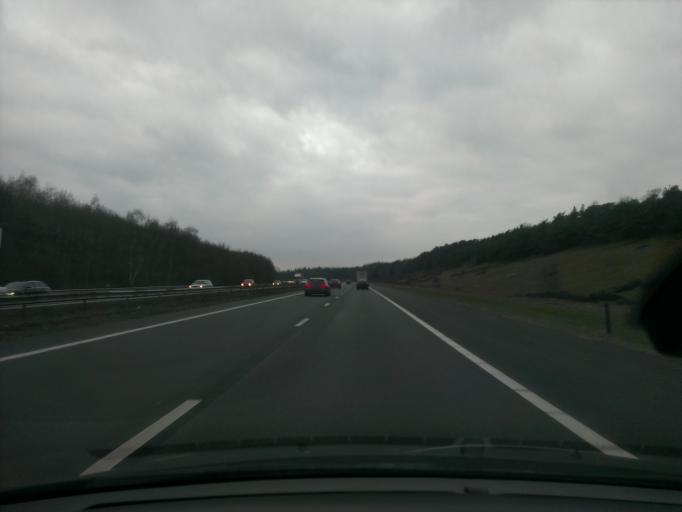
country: NL
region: Overijssel
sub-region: Gemeente Hof van Twente
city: Markelo
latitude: 52.2836
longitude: 6.5345
